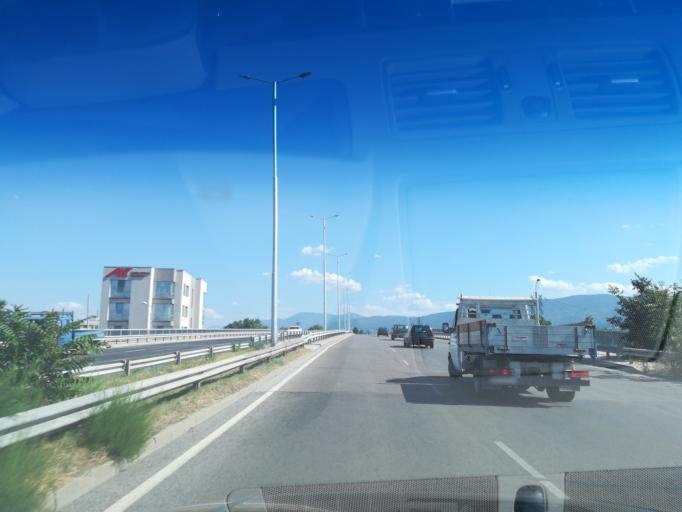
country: BG
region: Plovdiv
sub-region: Obshtina Plovdiv
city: Plovdiv
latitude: 42.1192
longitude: 24.7754
